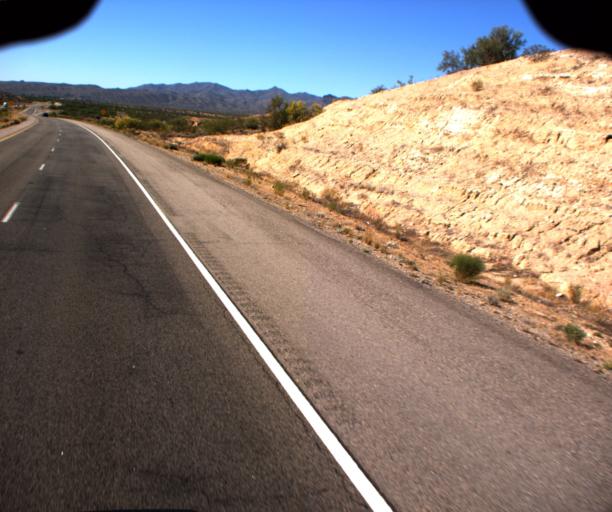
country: US
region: Arizona
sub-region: Yavapai County
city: Bagdad
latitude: 34.7482
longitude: -113.6166
